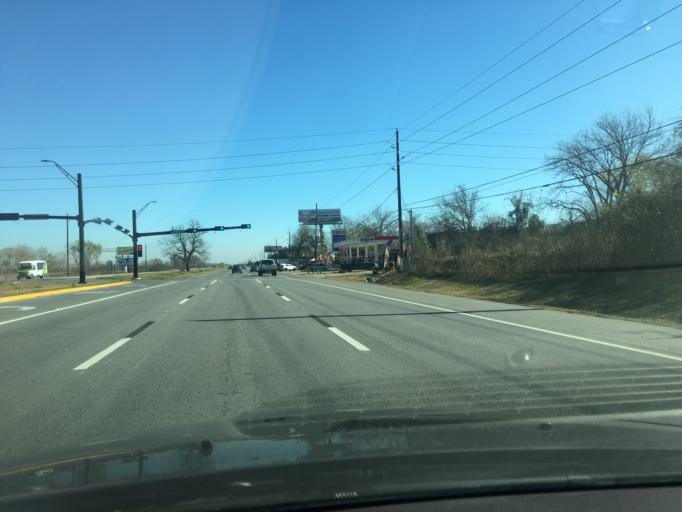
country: US
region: Texas
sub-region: Fort Bend County
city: Richmond
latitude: 29.5963
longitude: -95.7346
